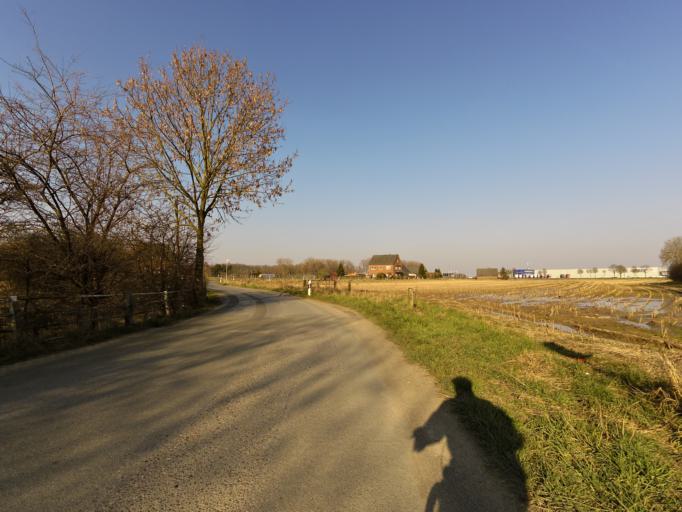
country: DE
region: North Rhine-Westphalia
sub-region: Regierungsbezirk Dusseldorf
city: Emmerich
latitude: 51.8461
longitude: 6.2635
